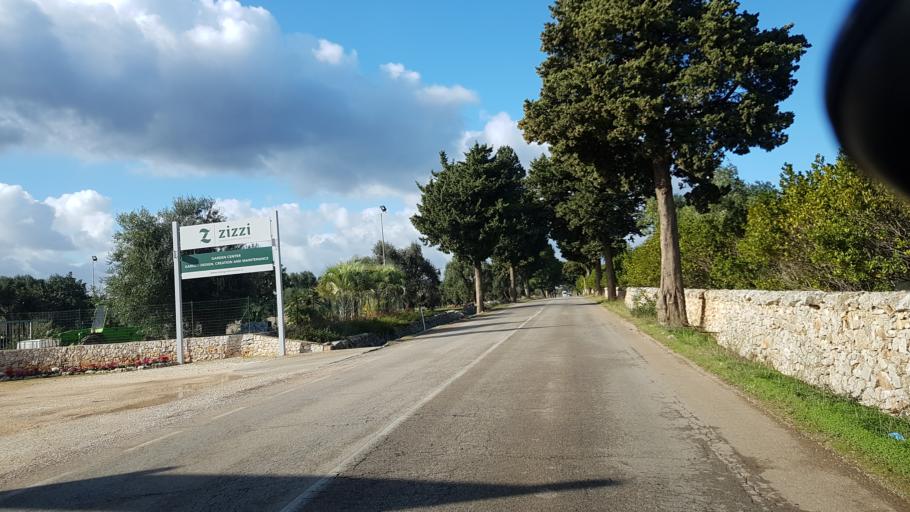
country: IT
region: Apulia
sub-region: Provincia di Brindisi
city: Pezze di Greco
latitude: 40.8007
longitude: 17.4398
